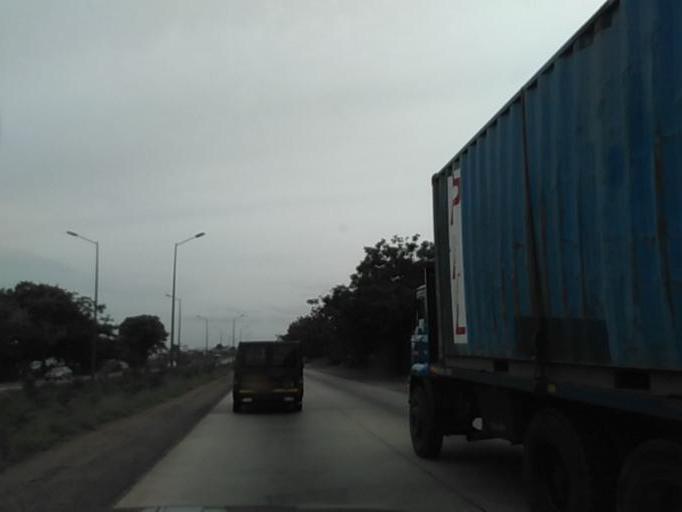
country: GH
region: Greater Accra
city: Medina Estates
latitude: 5.6394
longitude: -0.1325
